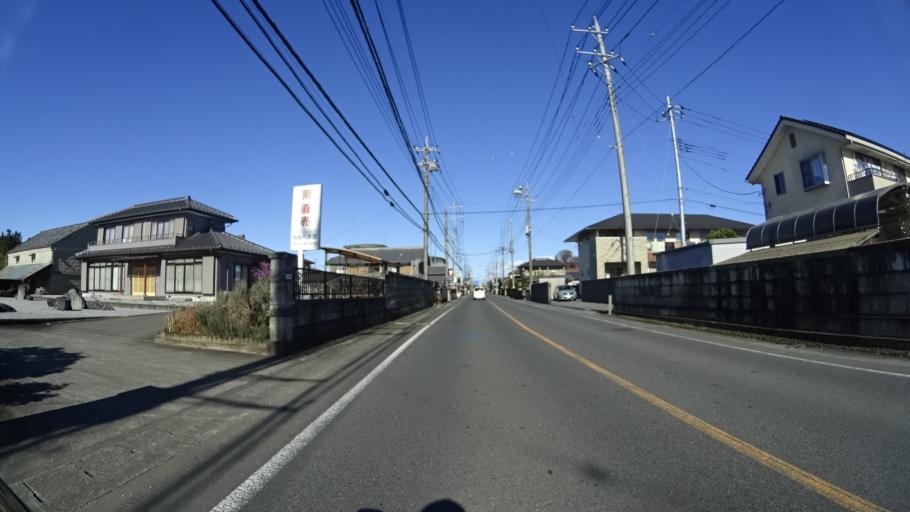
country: JP
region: Tochigi
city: Mibu
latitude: 36.4395
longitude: 139.7519
